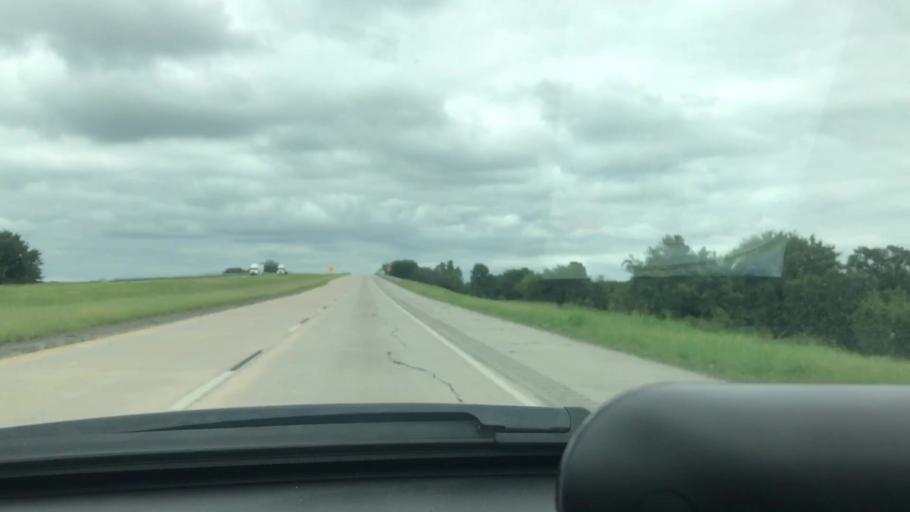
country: US
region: Oklahoma
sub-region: Wagoner County
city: Wagoner
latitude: 35.8793
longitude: -95.4033
